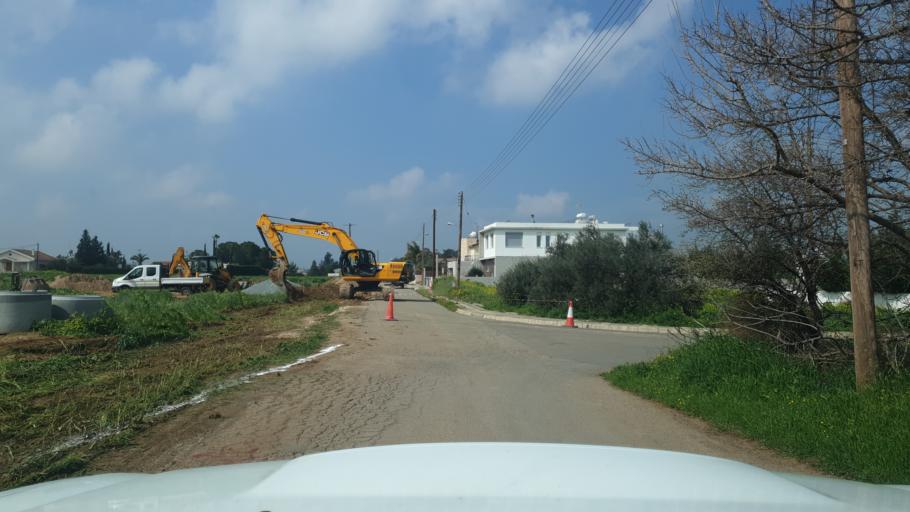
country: CY
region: Lefkosia
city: Kato Deftera
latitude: 35.0830
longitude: 33.2869
